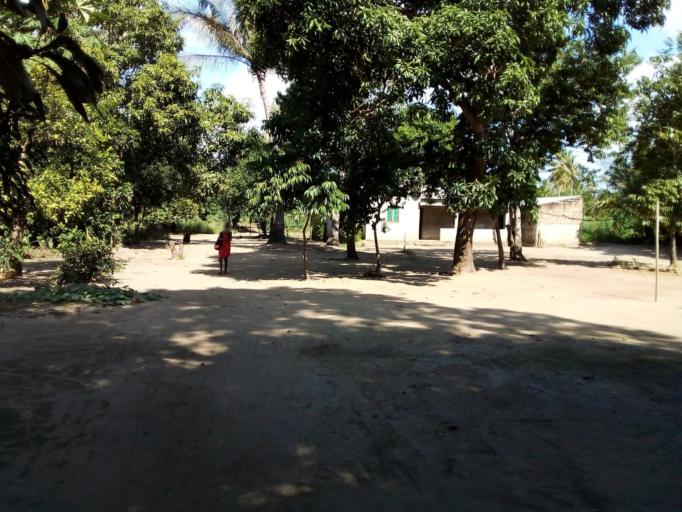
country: MZ
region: Zambezia
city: Quelimane
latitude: -17.5815
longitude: 36.6959
